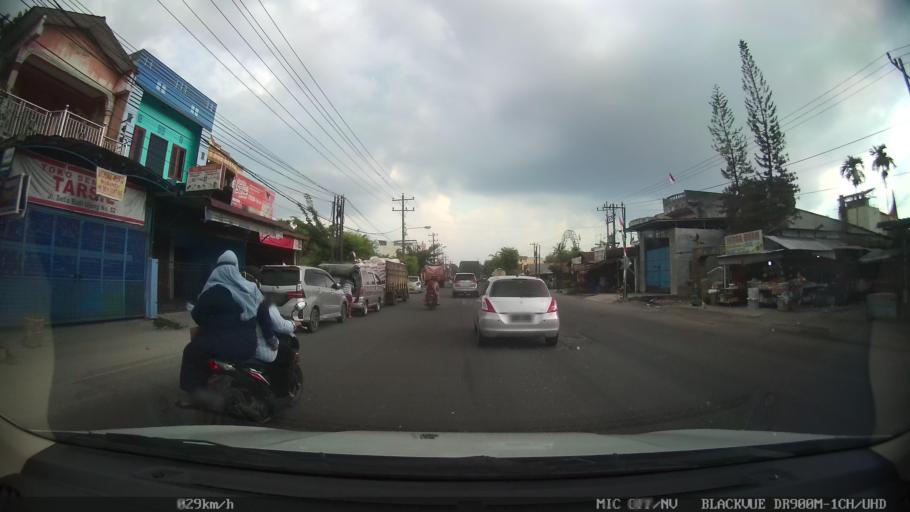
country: ID
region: North Sumatra
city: Sunggal
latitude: 3.5258
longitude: 98.6198
